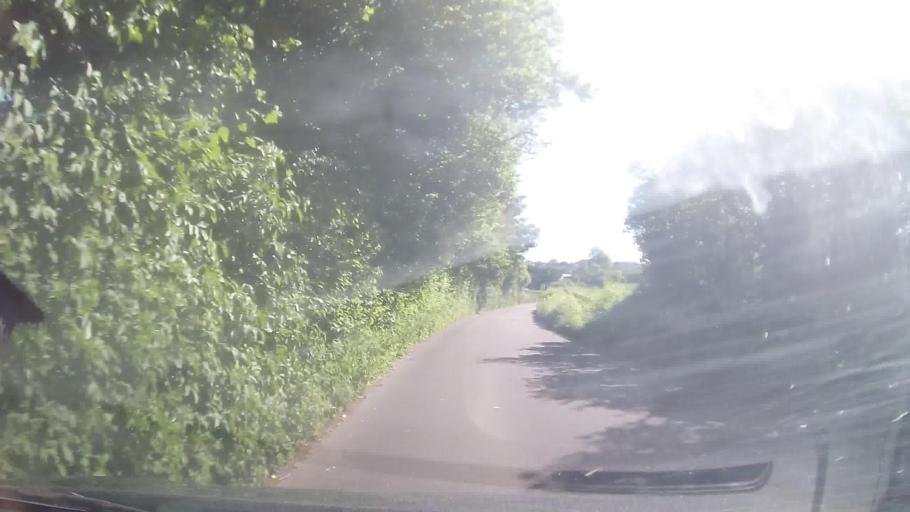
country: GB
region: England
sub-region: Borough of Torbay
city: Brixham
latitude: 50.3770
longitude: -3.5345
